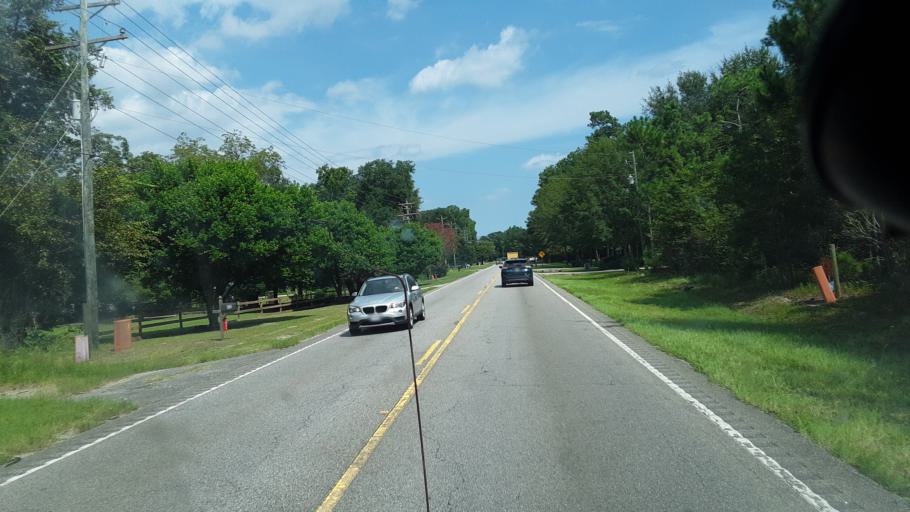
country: US
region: South Carolina
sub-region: Horry County
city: Red Hill
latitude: 33.8212
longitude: -78.9377
